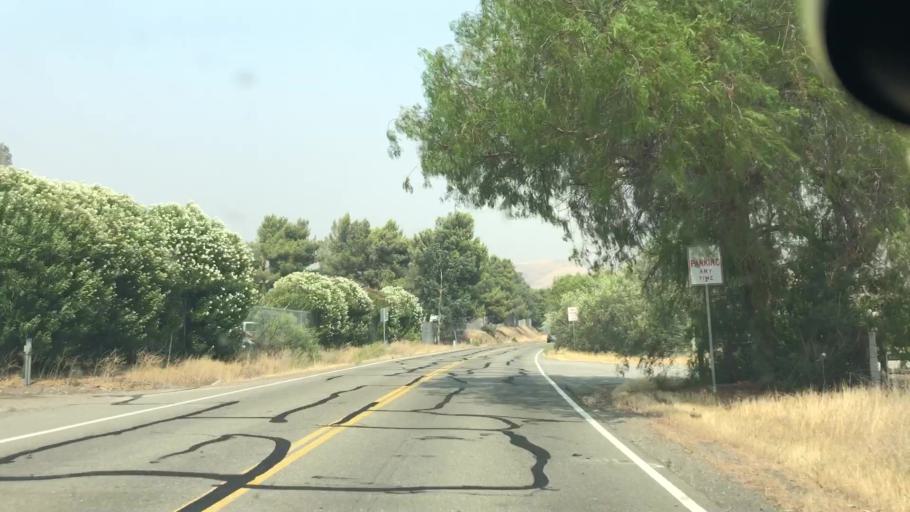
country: US
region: California
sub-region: San Joaquin County
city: Tracy
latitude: 37.6335
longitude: -121.5014
